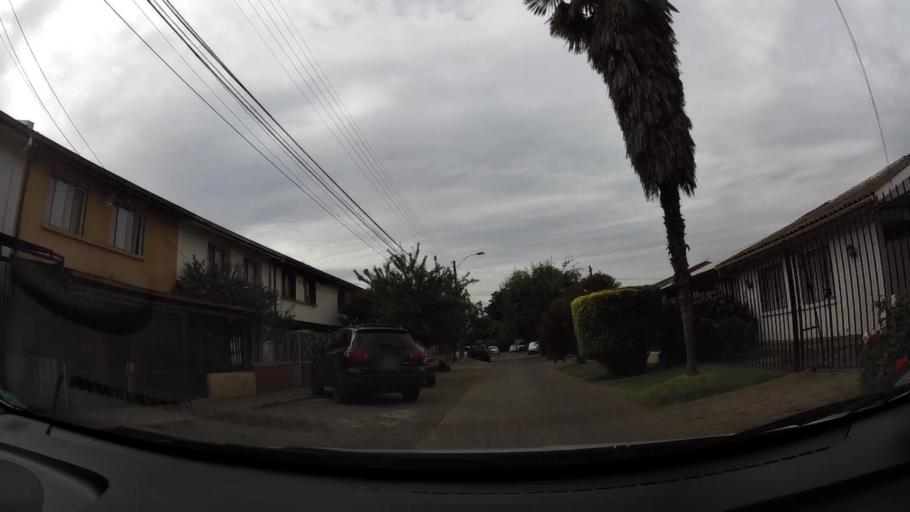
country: CL
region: O'Higgins
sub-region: Provincia de Cachapoal
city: Rancagua
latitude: -34.1591
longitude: -70.7396
